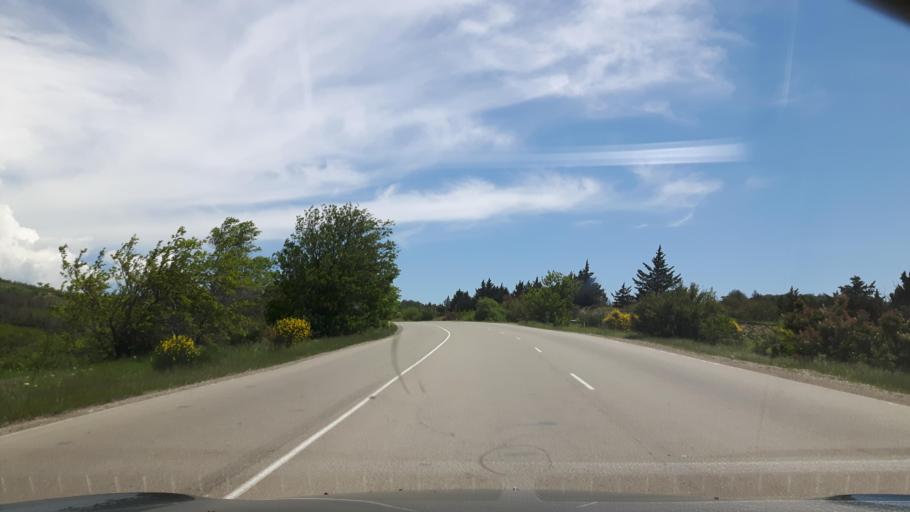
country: GE
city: Didi Lilo
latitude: 41.6927
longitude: 45.0778
